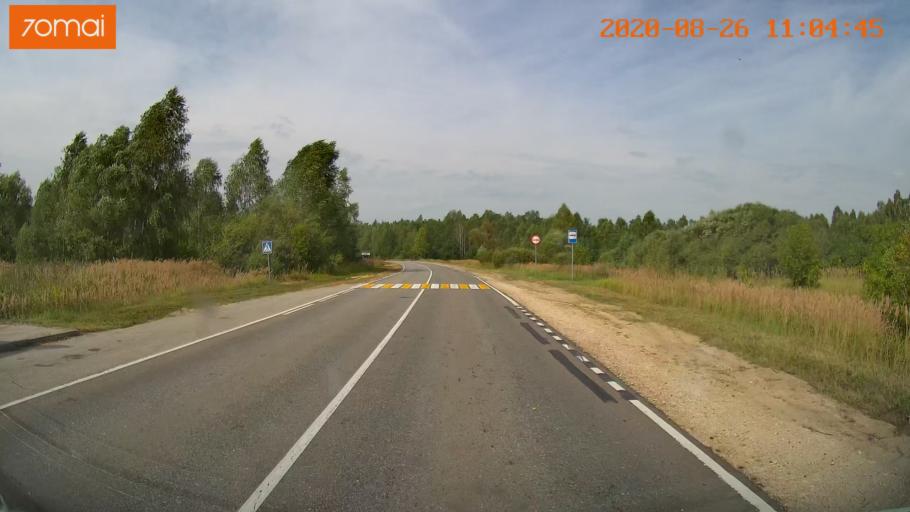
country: RU
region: Rjazan
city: Izhevskoye
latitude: 54.5293
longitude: 41.1890
